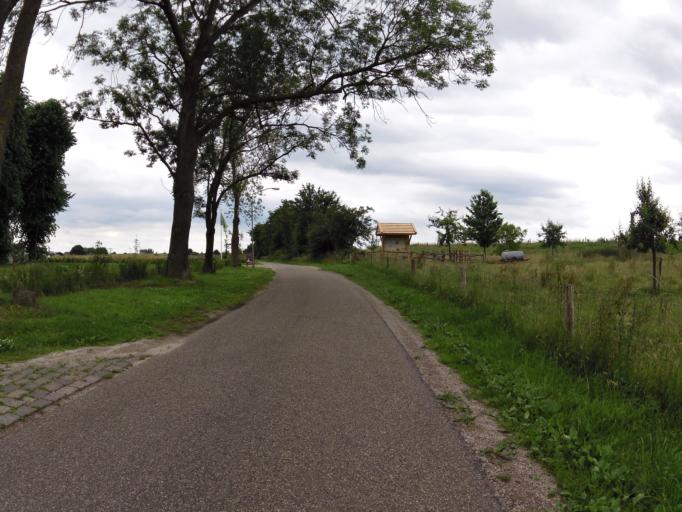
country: NL
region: North Brabant
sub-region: Gemeente Landerd
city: Reek
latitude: 51.7700
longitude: 5.6872
